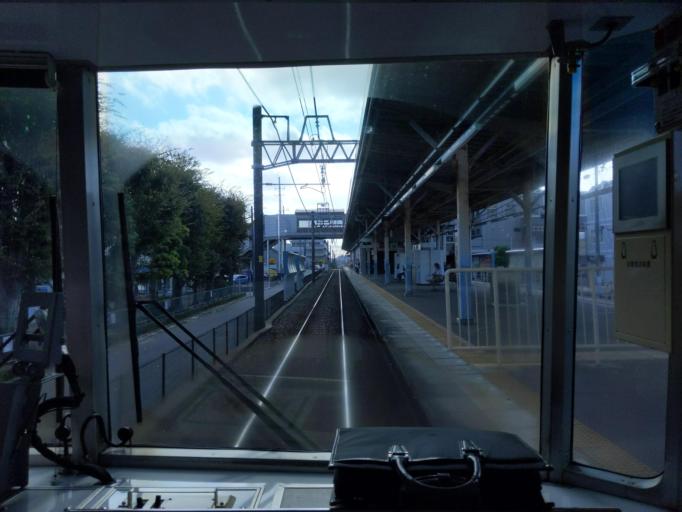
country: JP
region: Chiba
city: Funabashi
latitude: 35.7109
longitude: 140.0388
